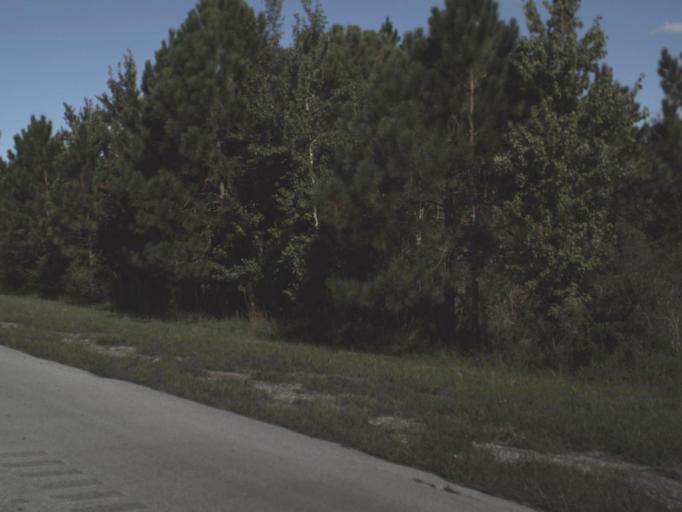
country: US
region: Florida
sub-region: Osceola County
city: Saint Cloud
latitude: 27.9453
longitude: -81.0819
